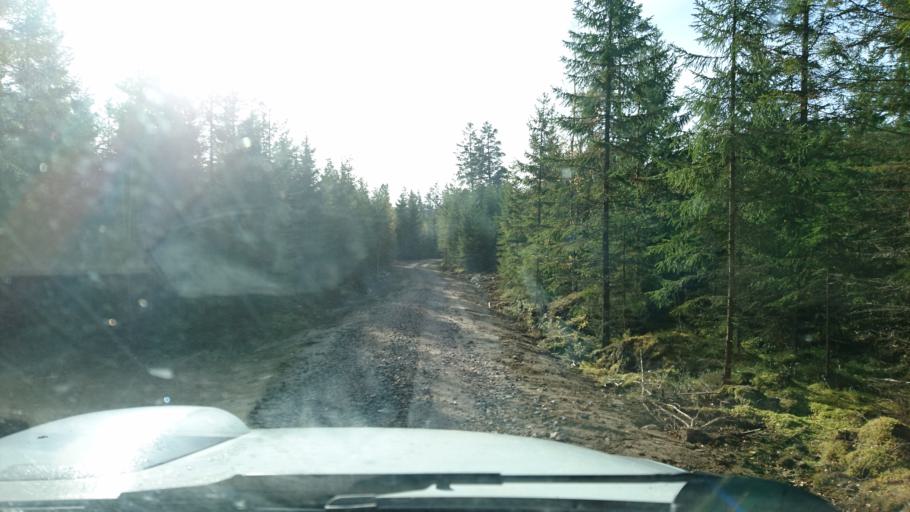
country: SE
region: Vaestra Goetaland
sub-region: Ulricehamns Kommun
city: Ulricehamn
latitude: 57.9401
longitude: 13.5514
